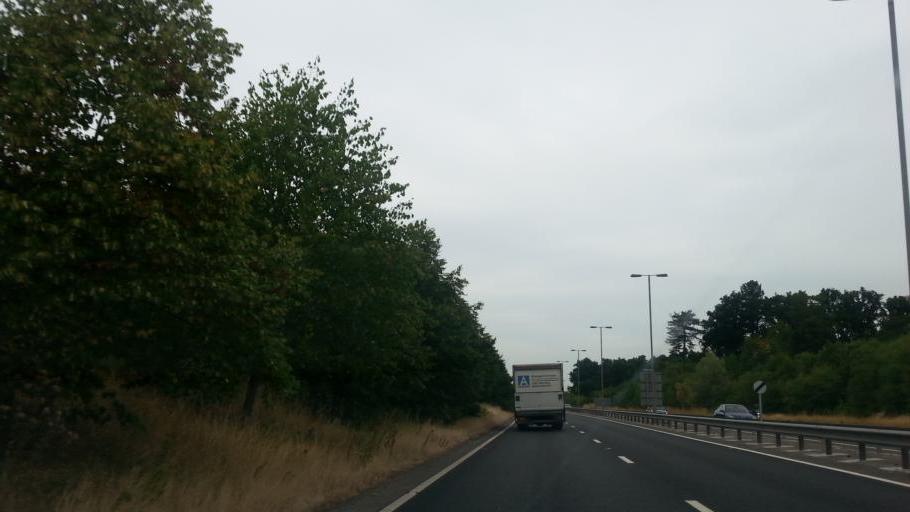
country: GB
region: England
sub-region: Derbyshire
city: Borrowash
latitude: 52.8882
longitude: -1.4060
